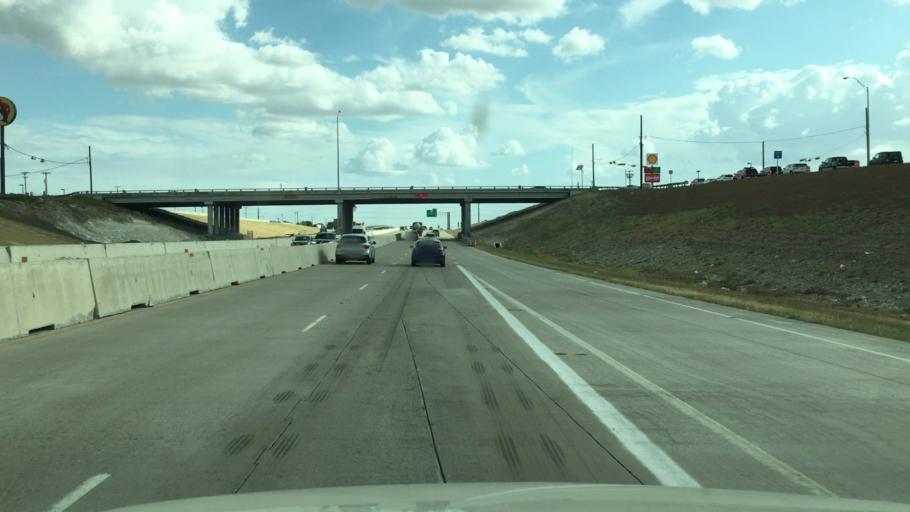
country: US
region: Texas
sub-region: Bell County
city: Temple
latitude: 31.1405
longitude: -97.3295
